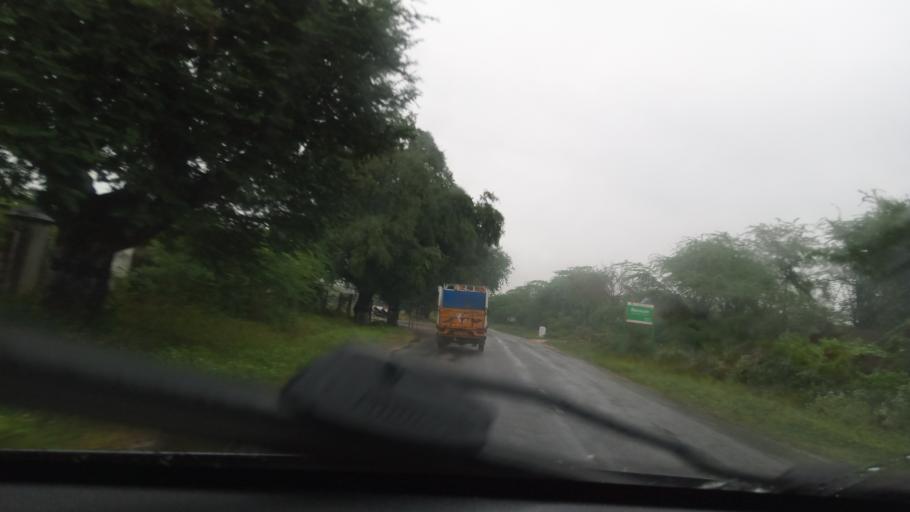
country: IN
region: Tamil Nadu
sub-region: Vellore
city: Walajapet
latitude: 12.8608
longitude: 79.3769
